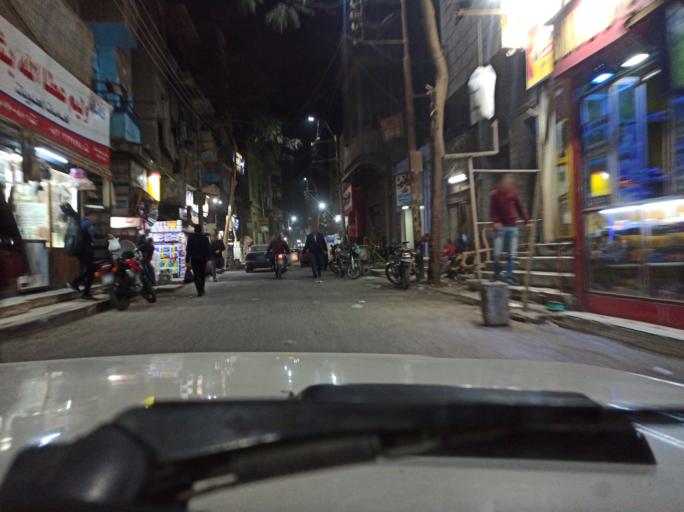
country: EG
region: Muhafazat Bani Suwayf
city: Bani Suwayf
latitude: 29.0738
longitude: 31.0935
